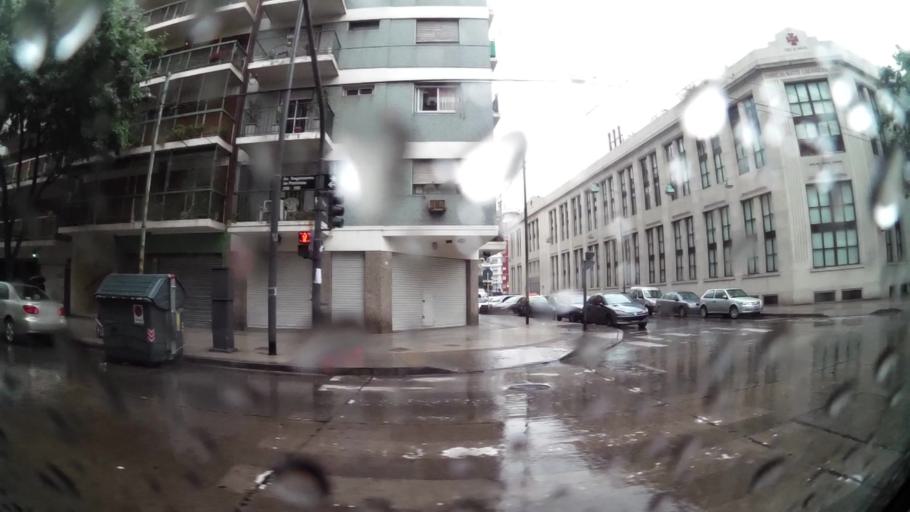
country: AR
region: Buenos Aires F.D.
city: Buenos Aires
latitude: -34.6310
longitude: -58.3706
